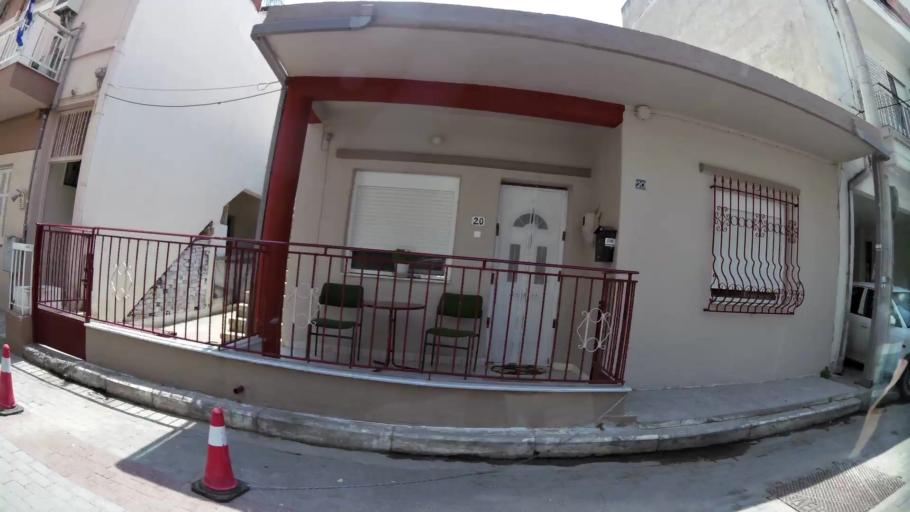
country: GR
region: Central Macedonia
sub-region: Nomos Thessalonikis
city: Evosmos
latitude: 40.6676
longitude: 22.9098
